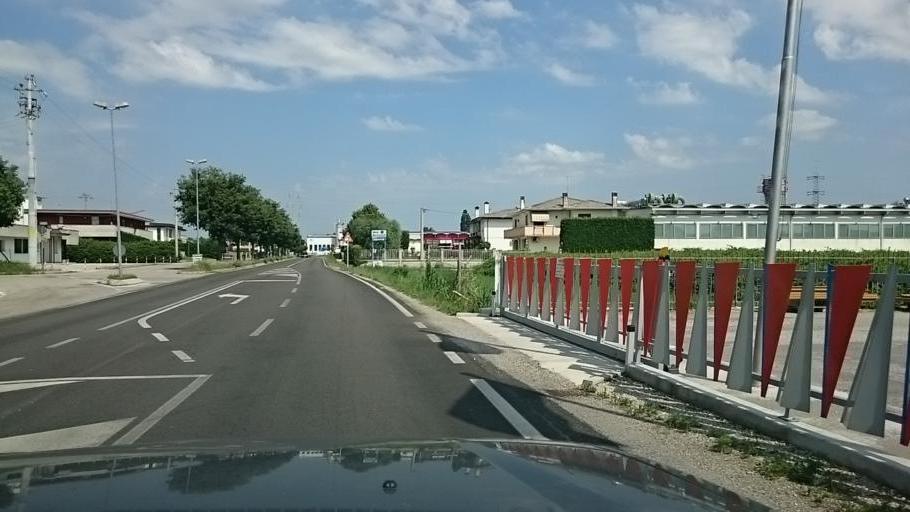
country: IT
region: Veneto
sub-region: Provincia di Vicenza
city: Cartigliano
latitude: 45.7207
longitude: 11.7271
